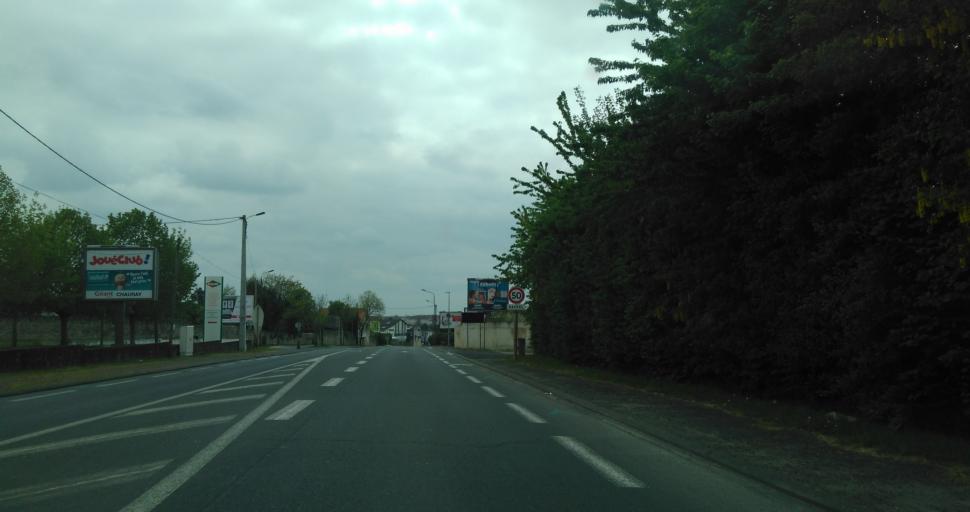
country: FR
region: Poitou-Charentes
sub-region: Departement des Deux-Sevres
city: Niort
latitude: 46.3434
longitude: -0.4445
